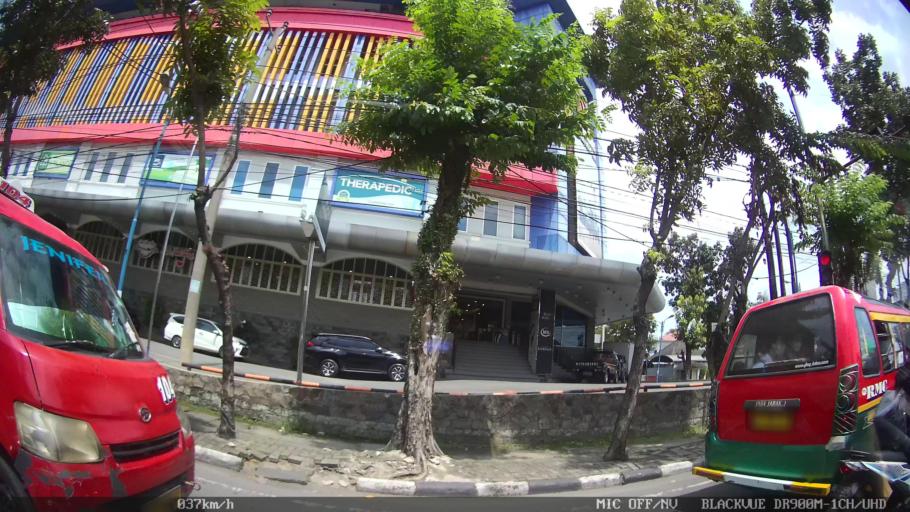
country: ID
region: North Sumatra
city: Medan
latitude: 3.5833
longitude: 98.6612
